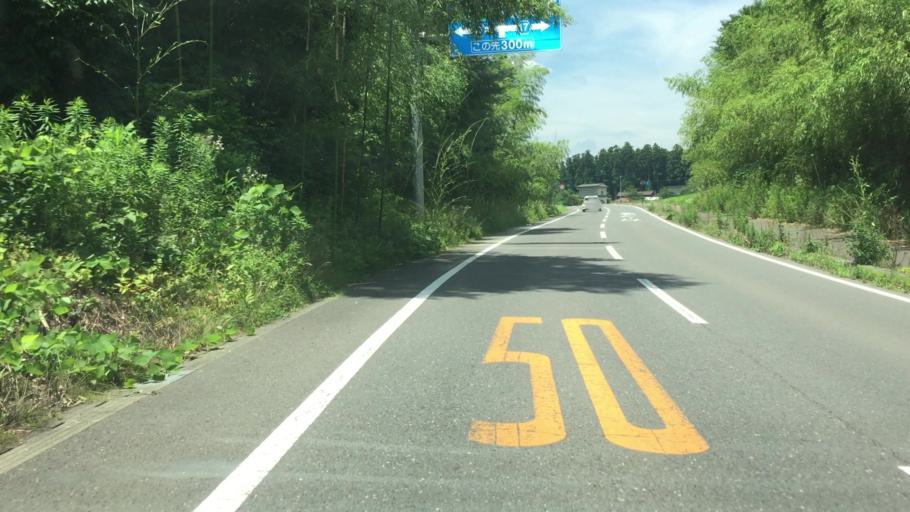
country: JP
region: Tochigi
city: Kuroiso
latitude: 37.0257
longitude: 140.0282
